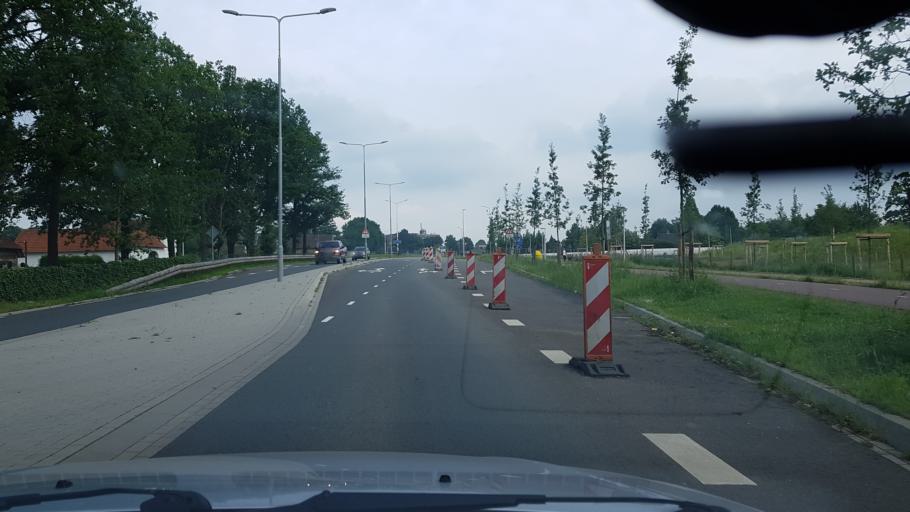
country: NL
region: Limburg
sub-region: Gemeente Schinnen
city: Amstenrade
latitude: 50.9376
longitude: 5.9275
